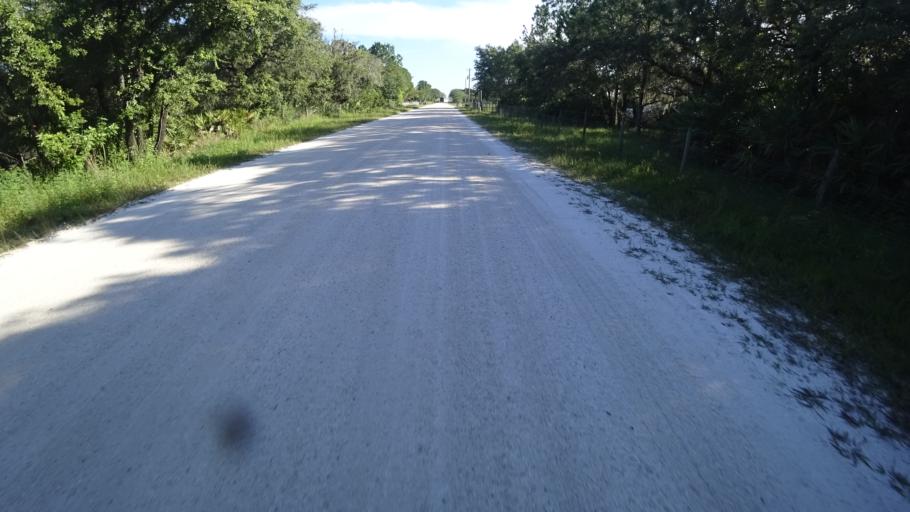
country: US
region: Florida
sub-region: Sarasota County
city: Fruitville
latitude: 27.4131
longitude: -82.2615
